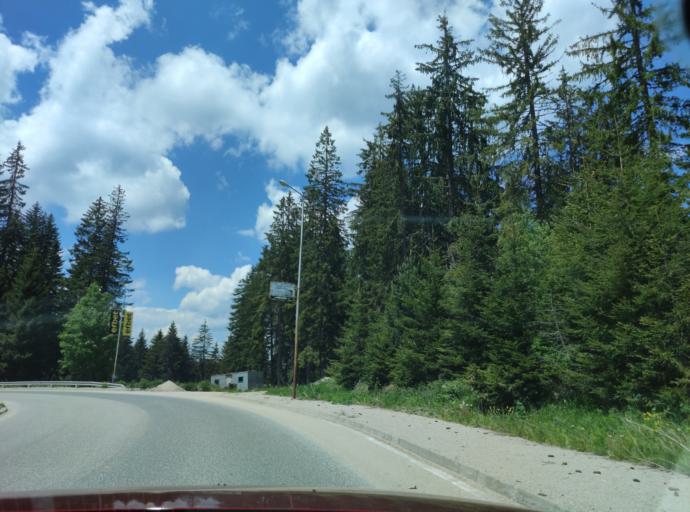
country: BG
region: Smolyan
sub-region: Obshtina Smolyan
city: Smolyan
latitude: 41.6386
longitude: 24.6979
